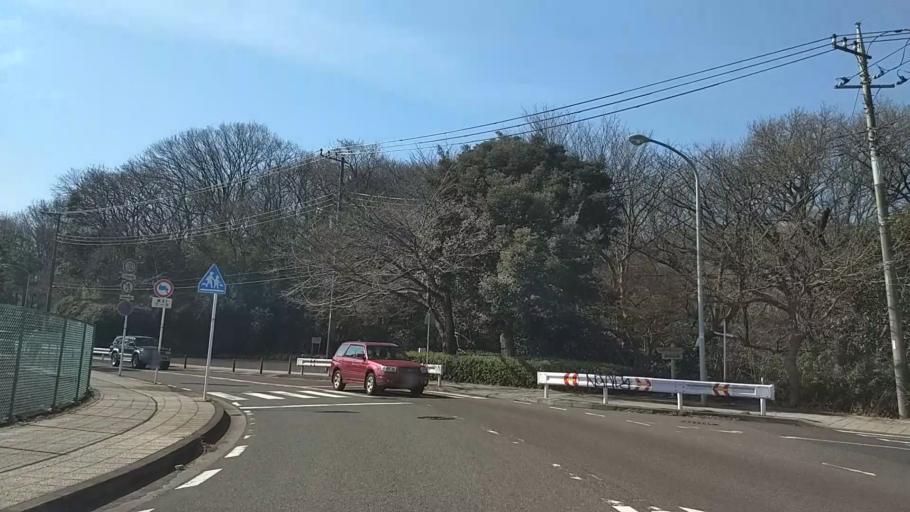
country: JP
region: Kanagawa
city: Kamakura
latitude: 35.3872
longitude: 139.5543
